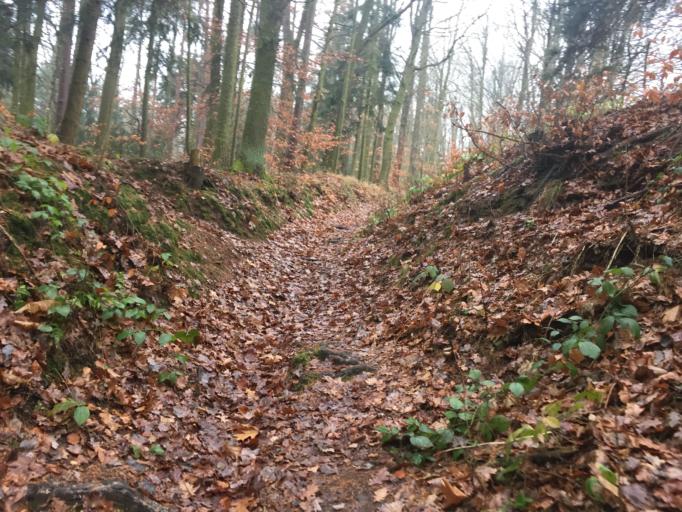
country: DE
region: Thuringia
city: Mockern
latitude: 50.8567
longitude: 11.7616
